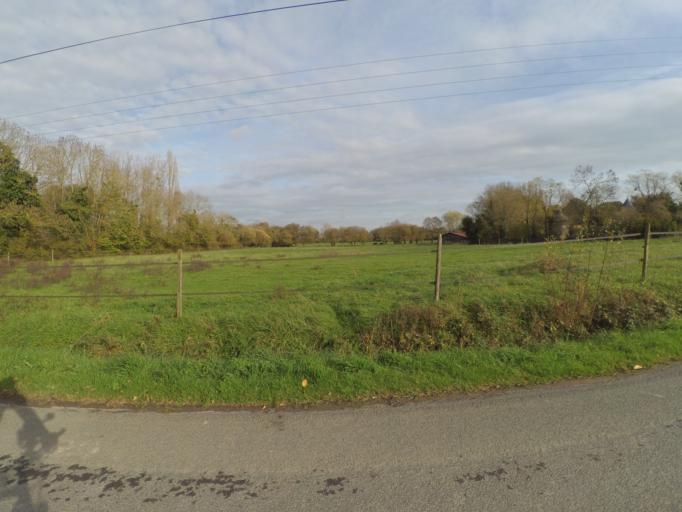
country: FR
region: Pays de la Loire
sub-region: Departement de la Vendee
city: Saint-Hilaire-de-Loulay
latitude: 47.0387
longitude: -1.3370
